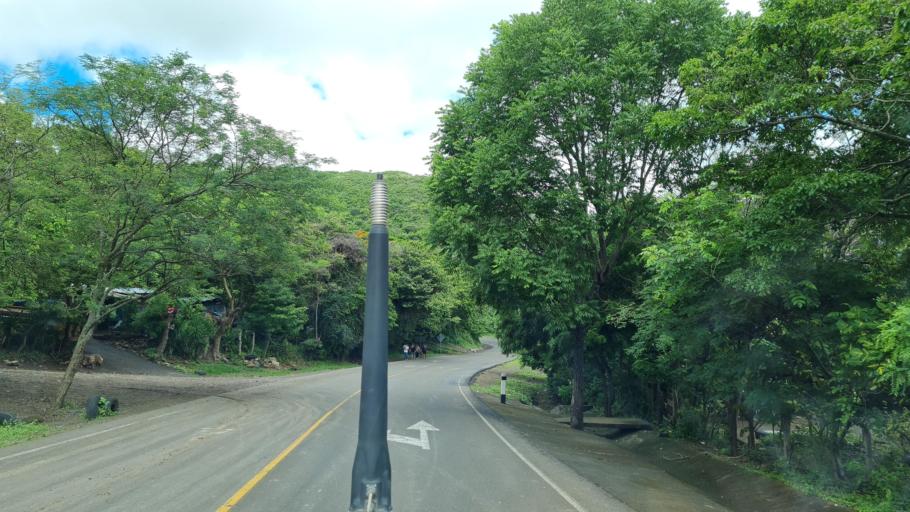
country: NI
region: Matagalpa
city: Terrabona
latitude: 12.5905
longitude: -85.9397
